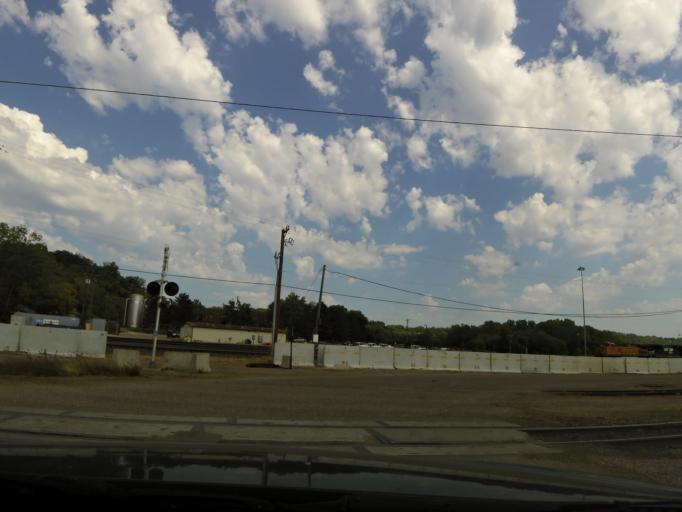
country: US
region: Minnesota
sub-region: Ramsey County
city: Saint Paul
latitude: 44.9427
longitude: -93.0518
